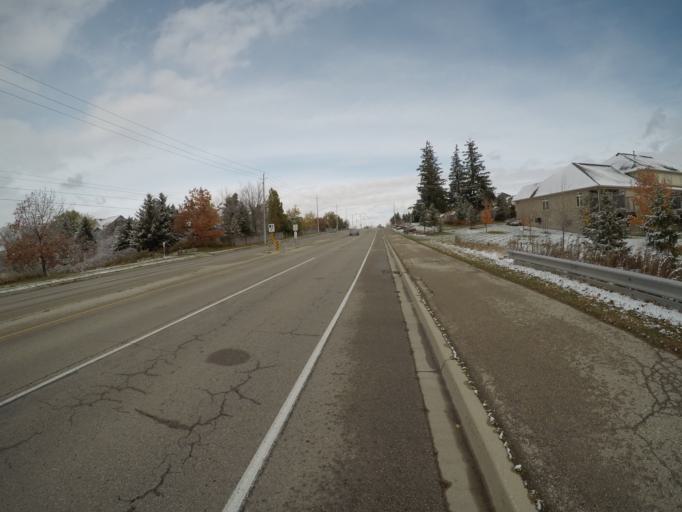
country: CA
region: Ontario
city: Waterloo
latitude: 43.5086
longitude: -80.4974
